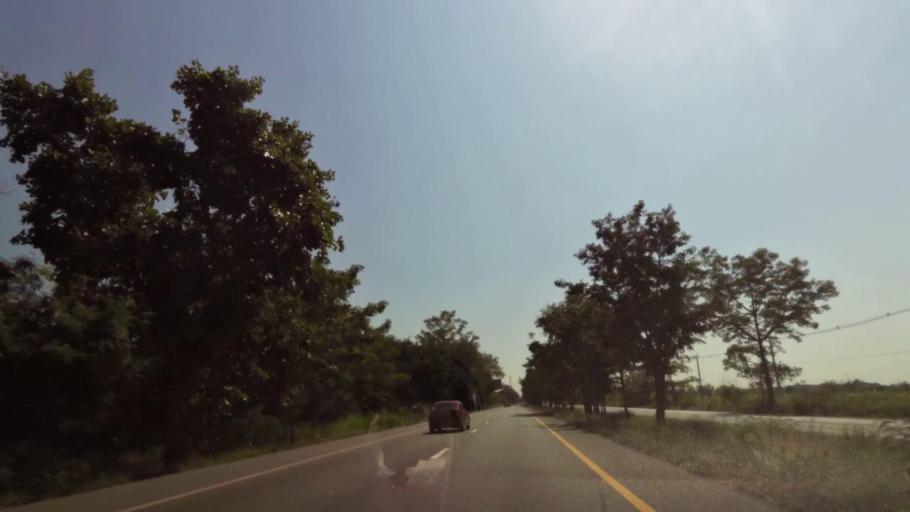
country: TH
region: Nakhon Sawan
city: Kao Liao
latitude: 15.8820
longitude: 100.1155
